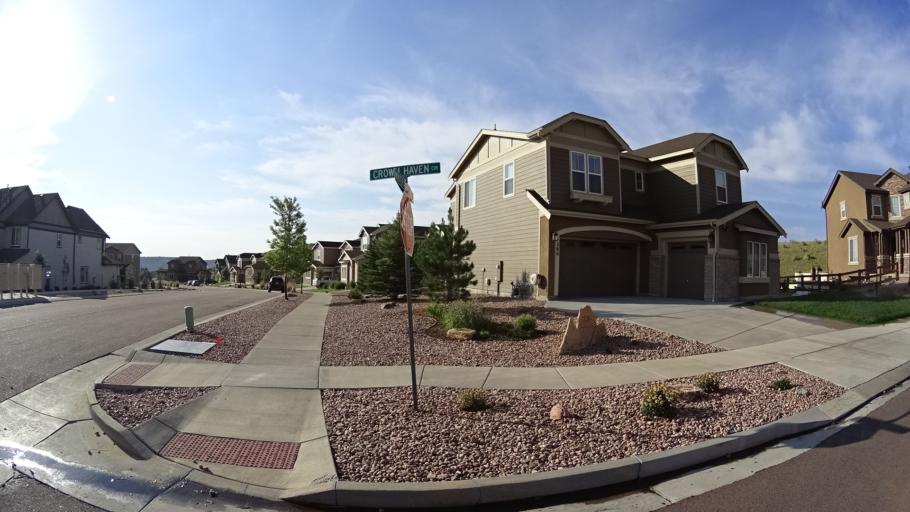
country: US
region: Colorado
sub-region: El Paso County
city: Air Force Academy
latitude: 38.9228
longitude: -104.8473
